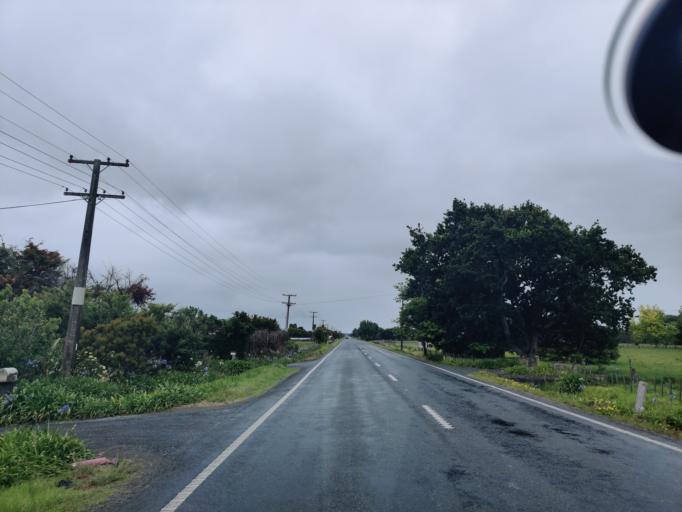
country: NZ
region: Northland
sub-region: Kaipara District
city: Dargaville
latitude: -35.9449
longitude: 173.8880
